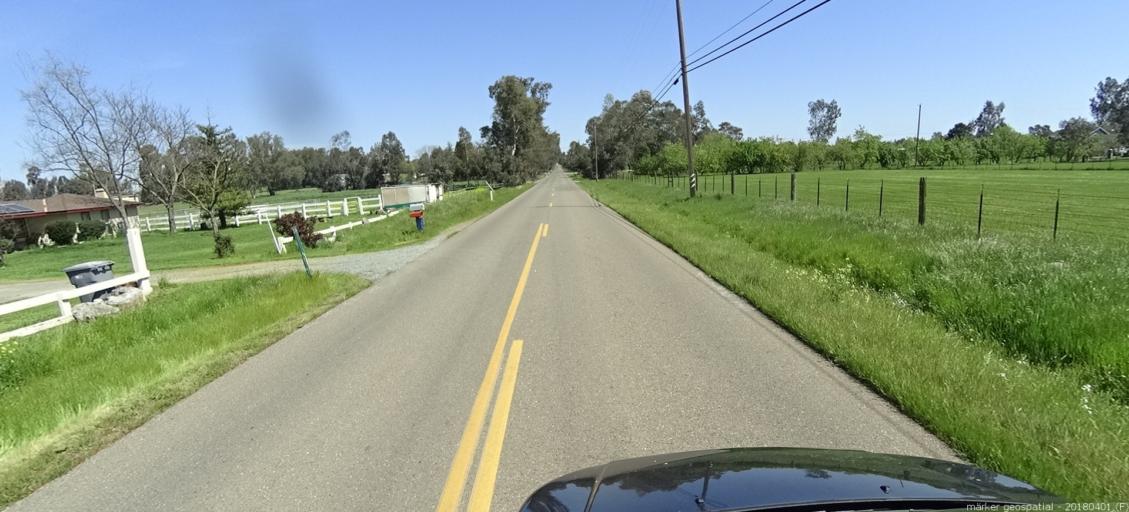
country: US
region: California
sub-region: Sacramento County
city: Wilton
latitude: 38.3869
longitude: -121.2320
